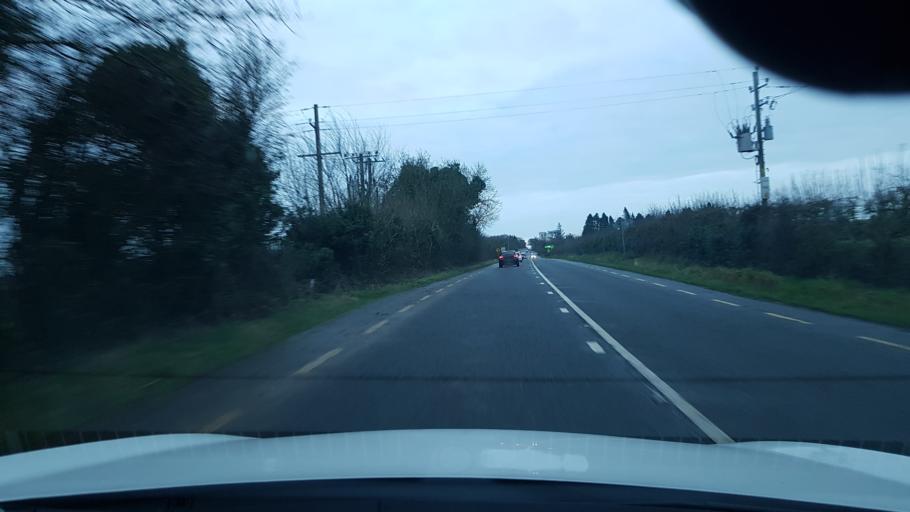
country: IE
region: Leinster
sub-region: An Mhi
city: Dunshaughlin
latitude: 53.5722
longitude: -6.5814
